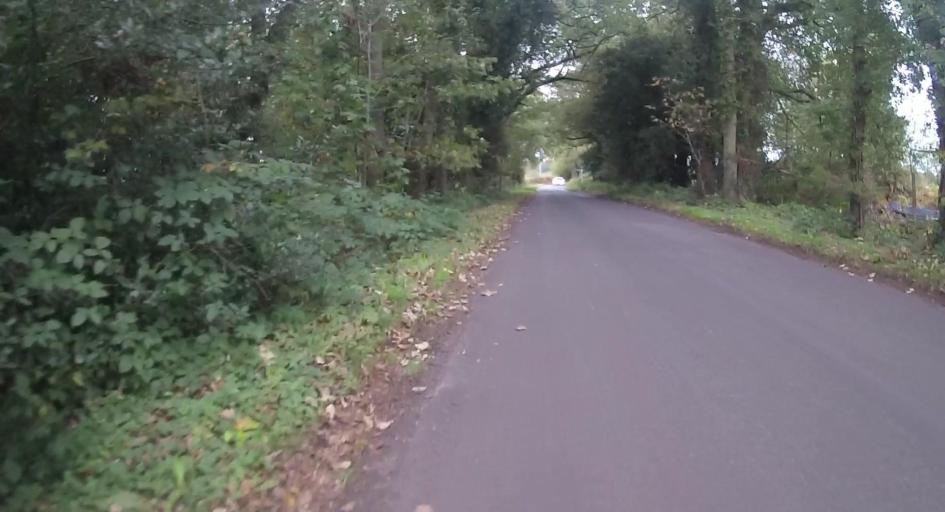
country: GB
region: England
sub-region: Hampshire
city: Fleet
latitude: 51.2819
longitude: -0.8808
